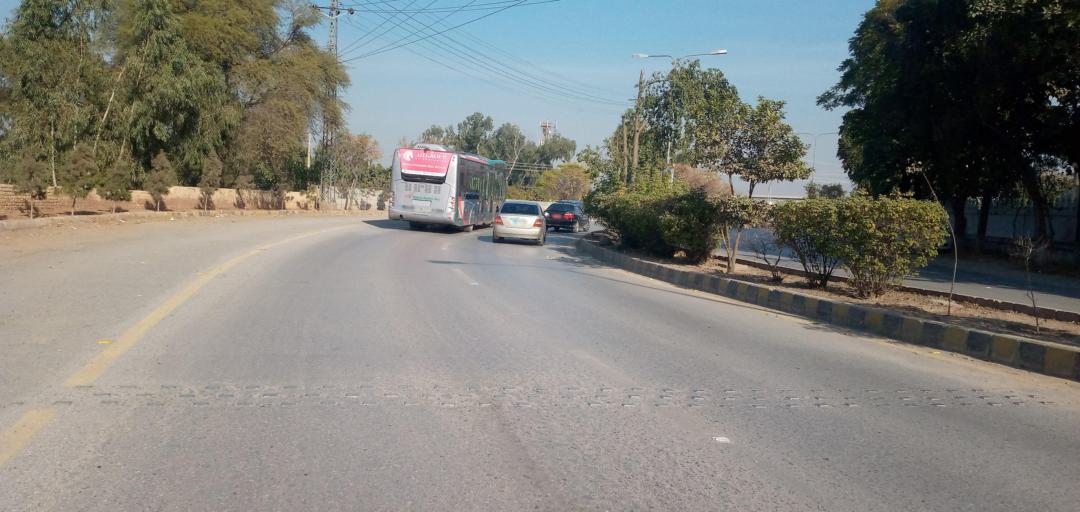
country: PK
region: Khyber Pakhtunkhwa
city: Peshawar
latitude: 33.9714
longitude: 71.4377
